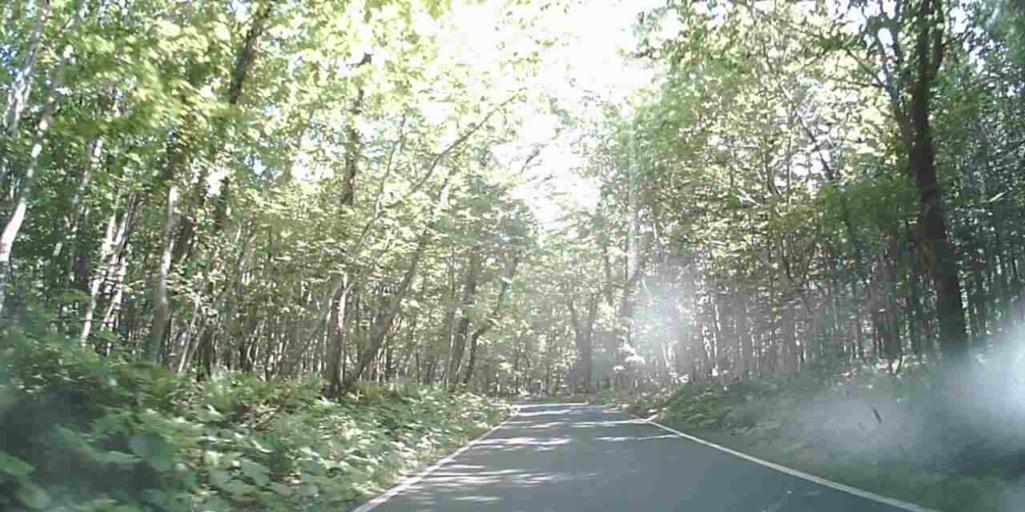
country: JP
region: Hokkaido
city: Shiraoi
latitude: 42.7345
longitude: 141.4106
